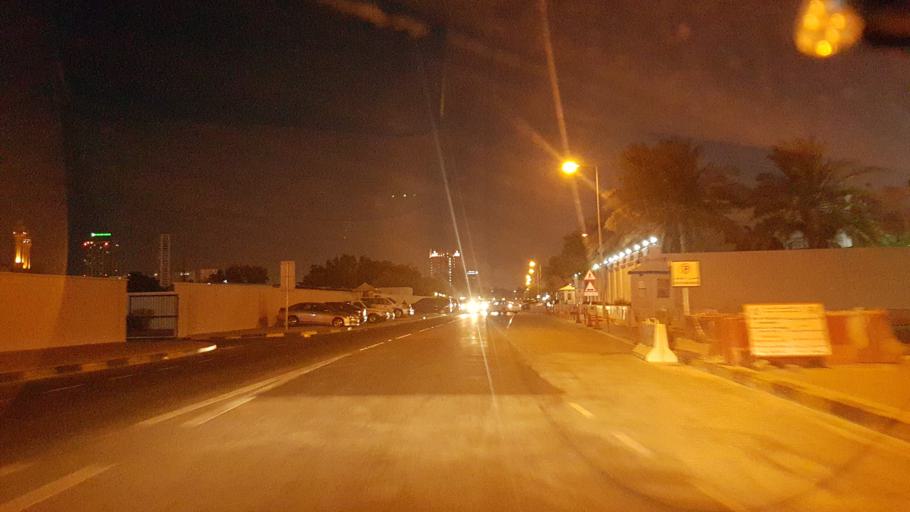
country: BH
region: Manama
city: Manama
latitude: 26.2240
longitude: 50.5951
